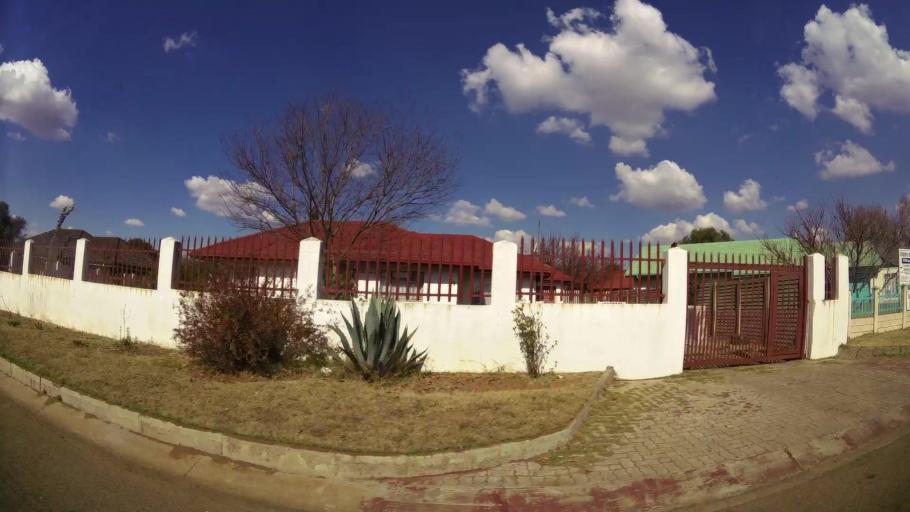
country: ZA
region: Mpumalanga
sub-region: Nkangala District Municipality
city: Witbank
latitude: -25.9440
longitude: 29.2457
